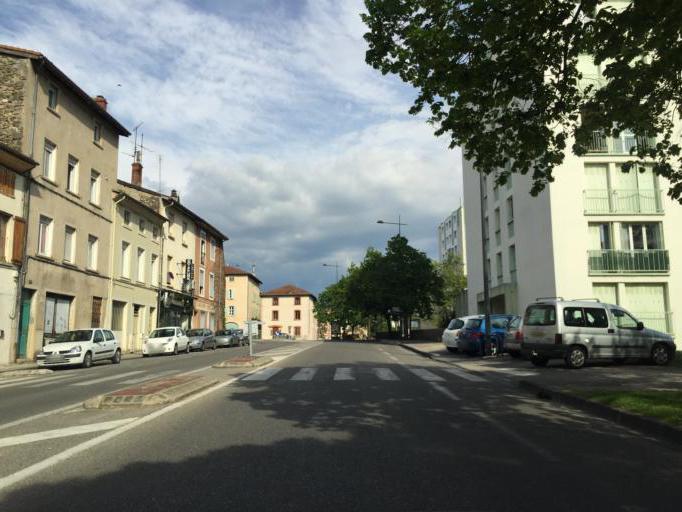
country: FR
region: Rhone-Alpes
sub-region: Departement de la Drome
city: Romans-sur-Isere
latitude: 45.0445
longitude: 5.0420
